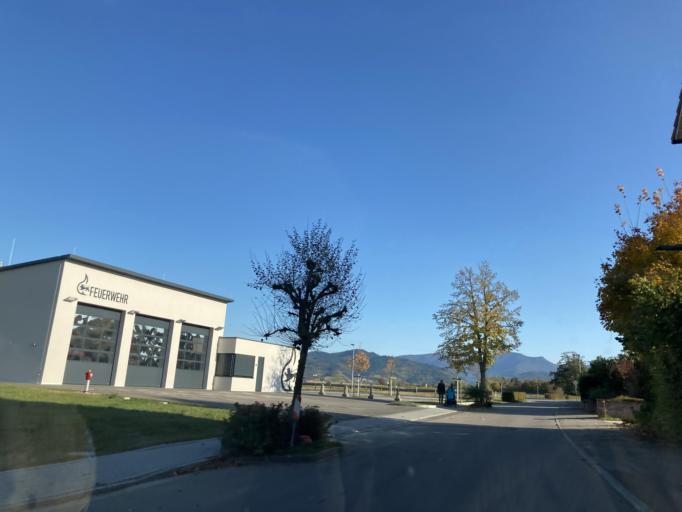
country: DE
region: Baden-Wuerttemberg
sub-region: Freiburg Region
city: Eschbach
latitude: 47.9008
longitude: 7.6720
